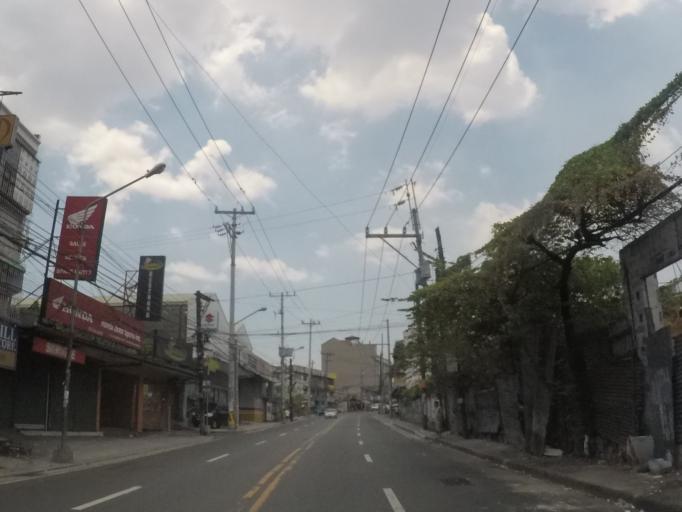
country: PH
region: Metro Manila
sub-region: San Juan
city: San Juan
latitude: 14.6089
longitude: 121.0288
